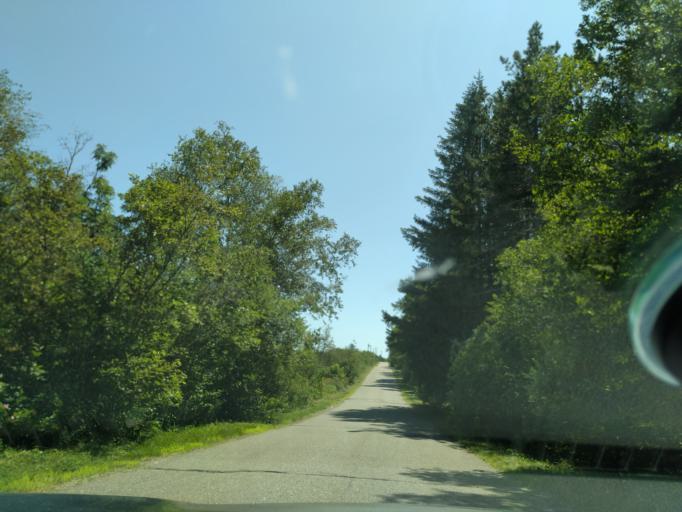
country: US
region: Maine
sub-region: Washington County
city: Eastport
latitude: 44.8328
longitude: -67.0078
